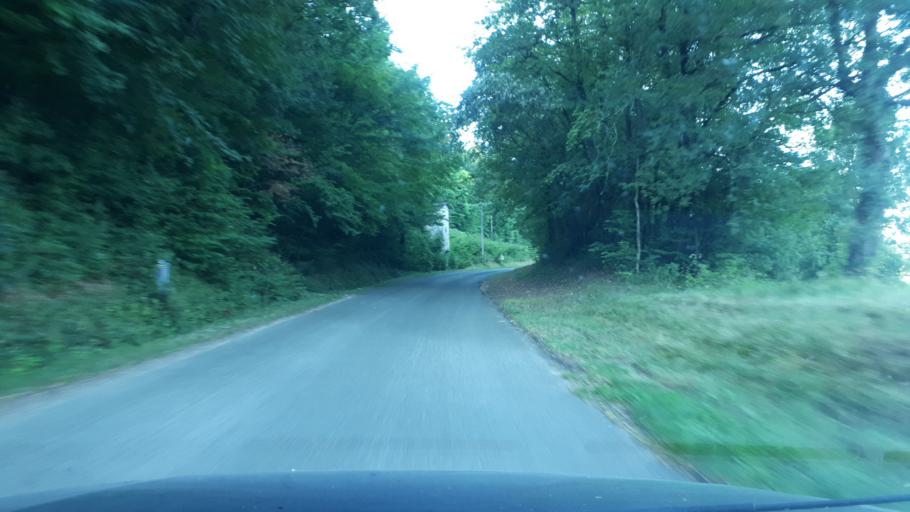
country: FR
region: Centre
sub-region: Departement du Loir-et-Cher
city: Villiers-sur-Loir
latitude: 47.7720
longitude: 0.9610
